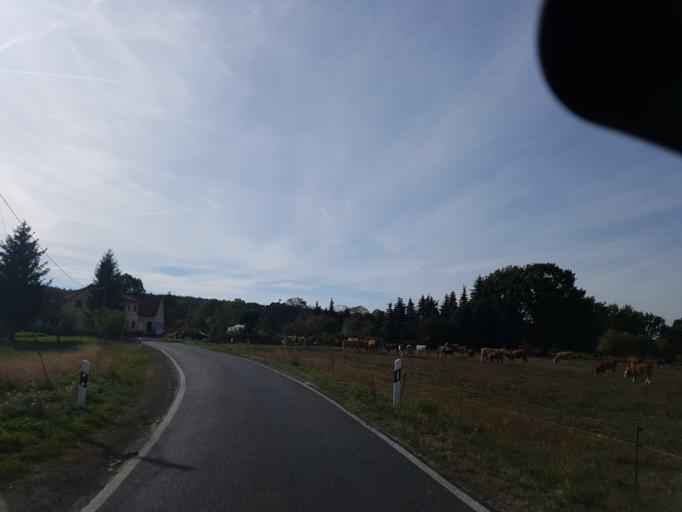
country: DE
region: Brandenburg
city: Ihlow
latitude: 51.8155
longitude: 13.2810
